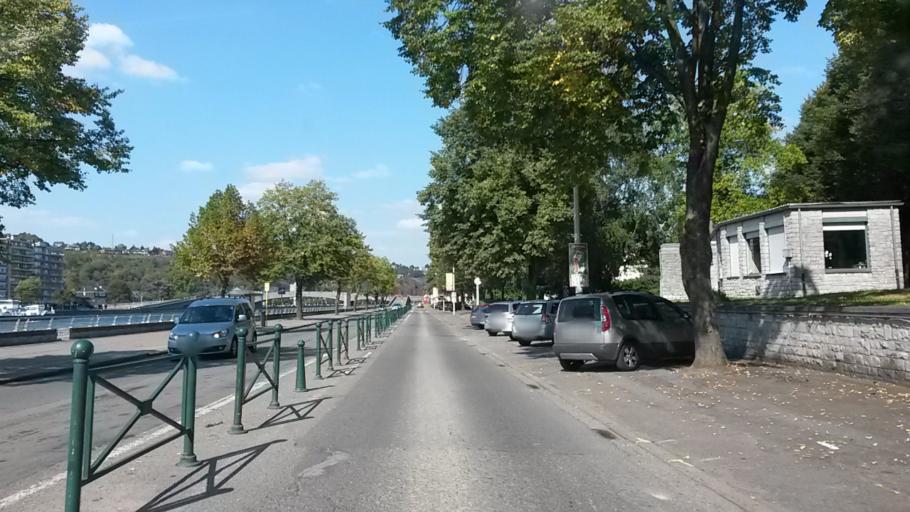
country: BE
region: Wallonia
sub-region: Province de Liege
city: Huy
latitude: 50.5211
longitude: 5.2395
